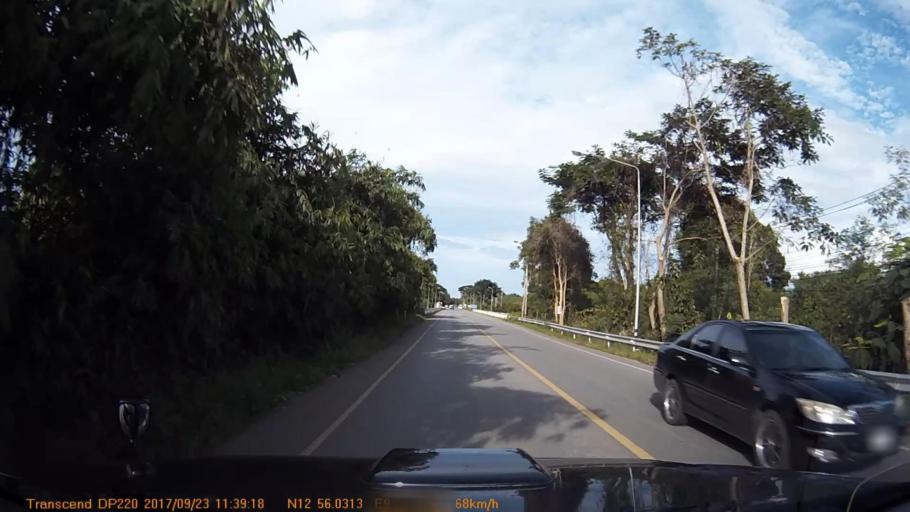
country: TH
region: Phetchaburi
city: Tha Yang
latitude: 12.9338
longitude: 99.7788
